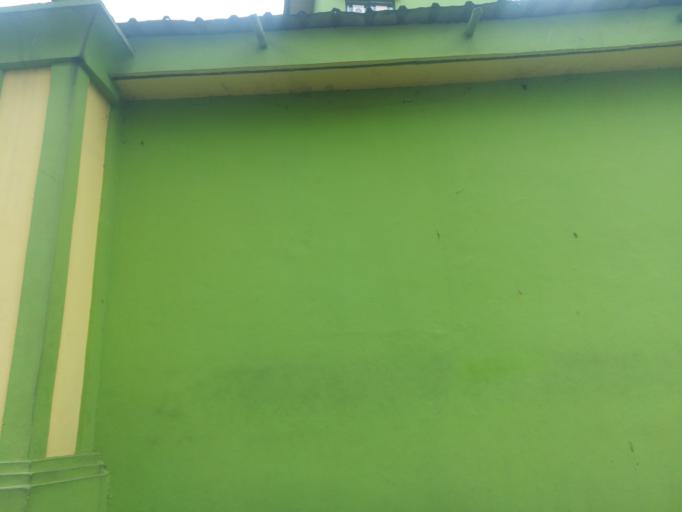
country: NG
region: Lagos
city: Ojota
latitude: 6.5757
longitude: 3.3727
